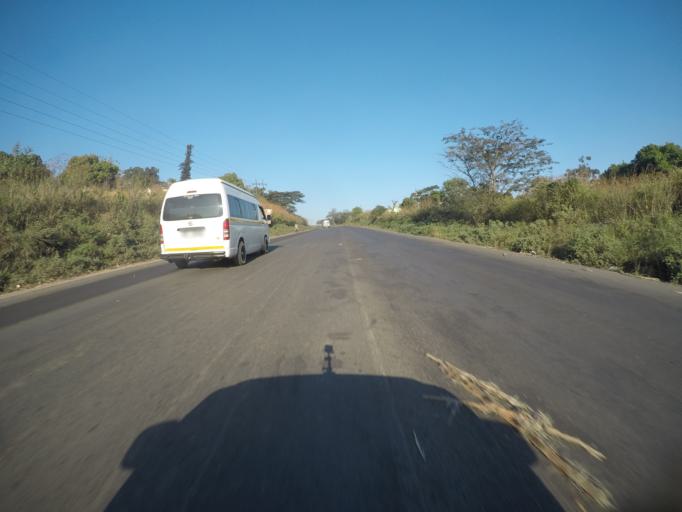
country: ZA
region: KwaZulu-Natal
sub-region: iLembe District Municipality
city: Stanger
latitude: -29.3870
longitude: 31.2525
